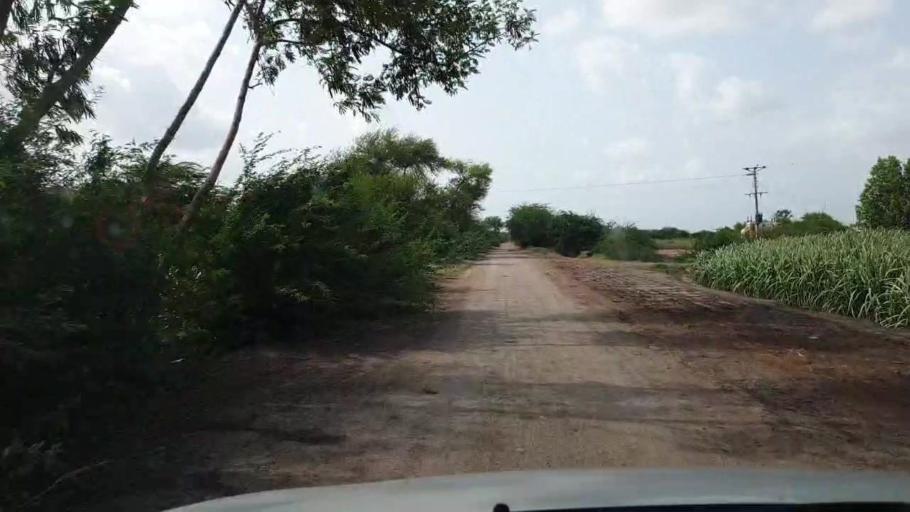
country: PK
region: Sindh
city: Kario
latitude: 24.7212
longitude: 68.6375
